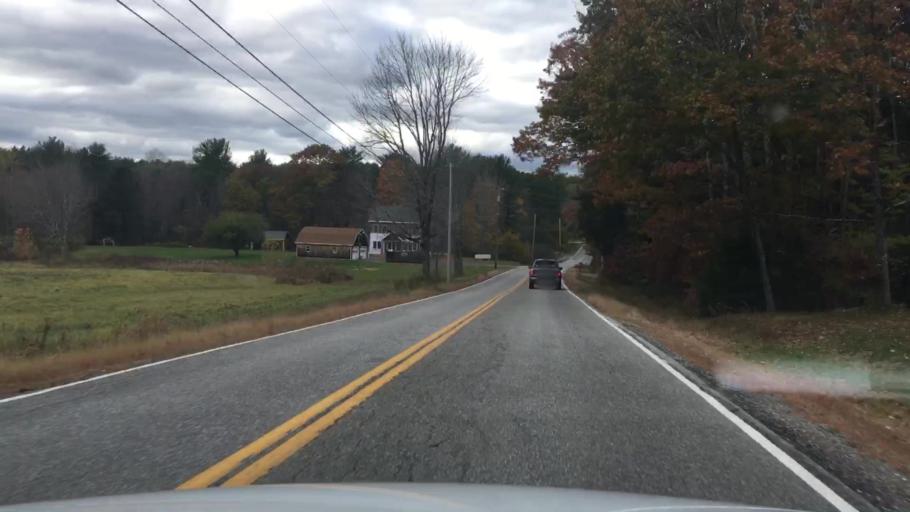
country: US
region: Maine
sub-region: Sagadahoc County
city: Richmond
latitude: 44.1280
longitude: -69.9088
